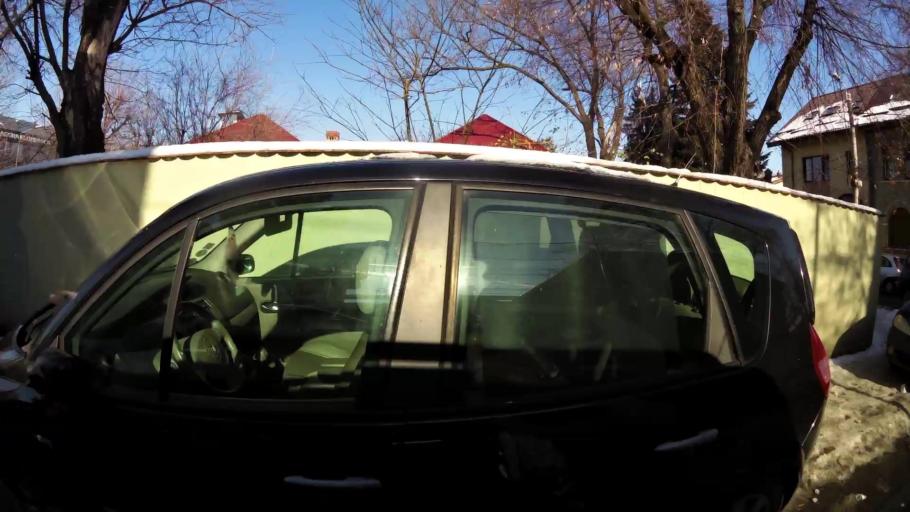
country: RO
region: Bucuresti
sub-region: Municipiul Bucuresti
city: Bucharest
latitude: 44.4601
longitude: 26.1014
